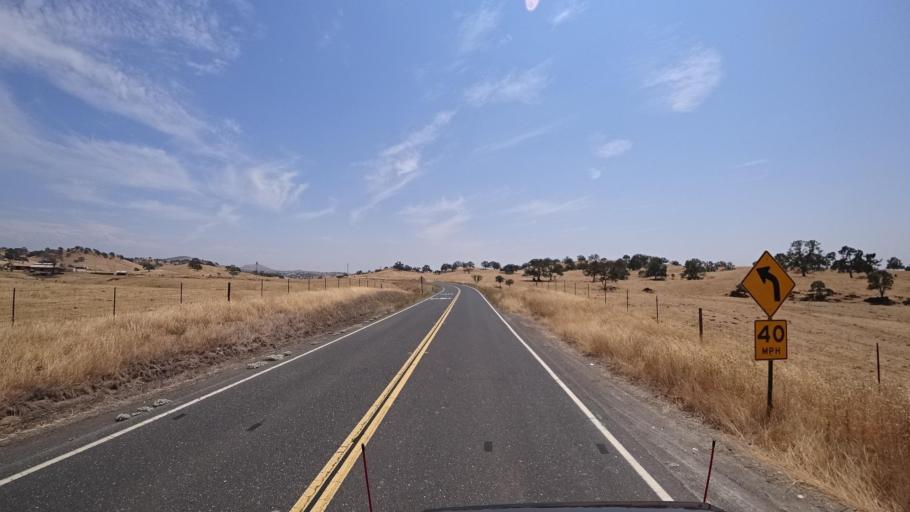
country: US
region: California
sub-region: Tuolumne County
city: Jamestown
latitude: 37.6417
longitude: -120.3765
